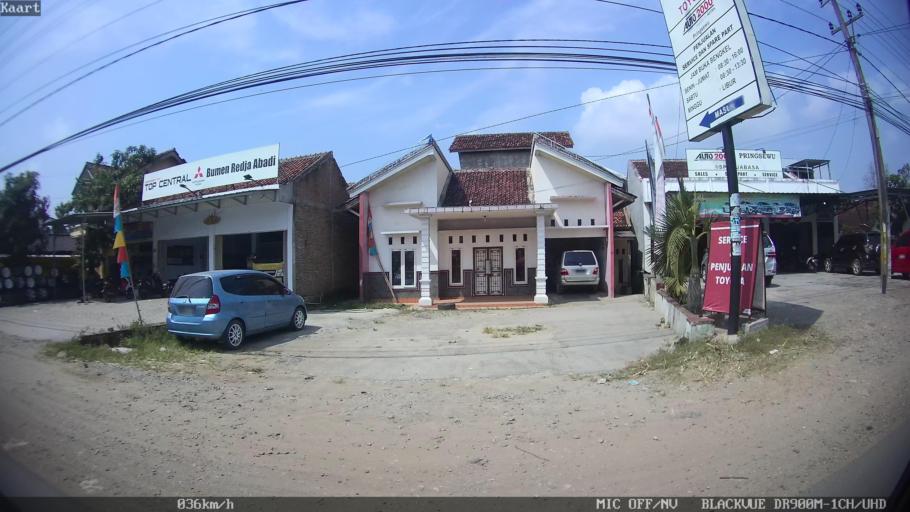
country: ID
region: Lampung
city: Pringsewu
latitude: -5.3616
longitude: 104.9968
